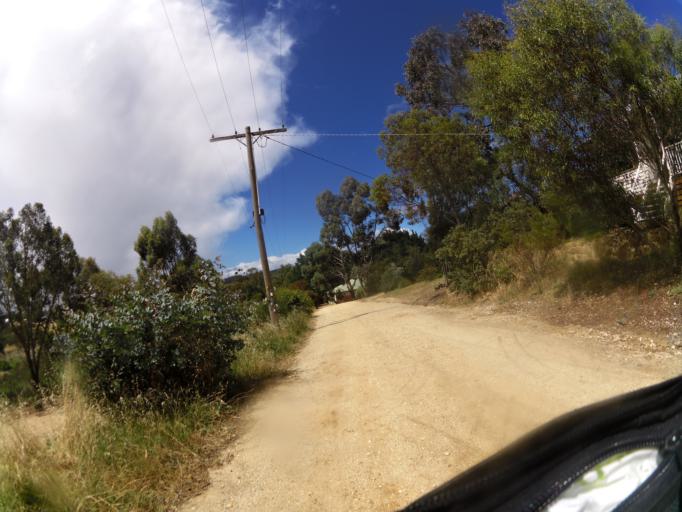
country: AU
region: Victoria
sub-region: Mount Alexander
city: Castlemaine
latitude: -37.0678
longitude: 144.2276
